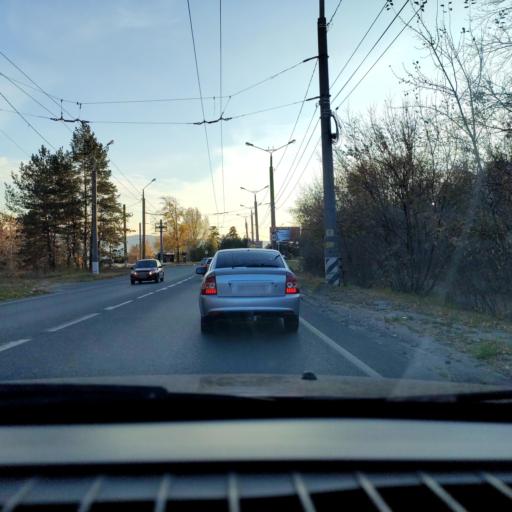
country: RU
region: Samara
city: Tol'yatti
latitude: 53.4772
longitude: 49.3494
